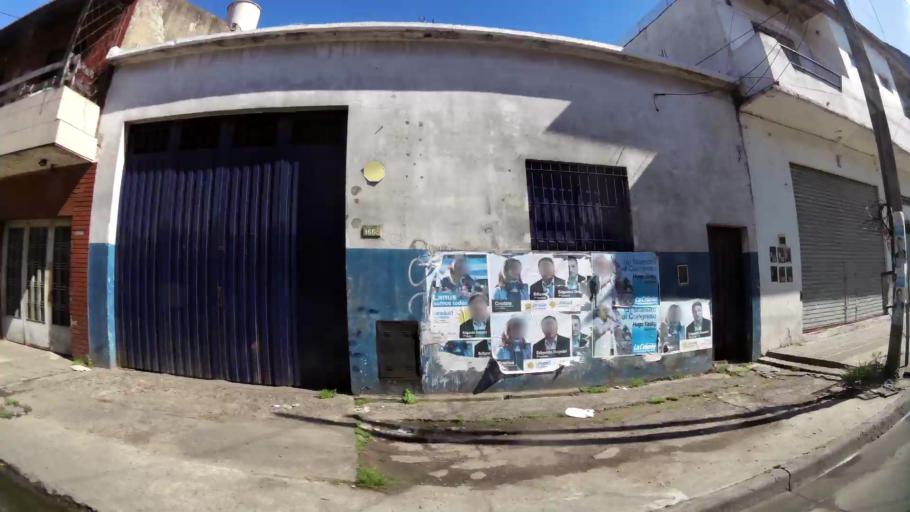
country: AR
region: Buenos Aires
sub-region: Partido de Lanus
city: Lanus
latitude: -34.6712
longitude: -58.4221
